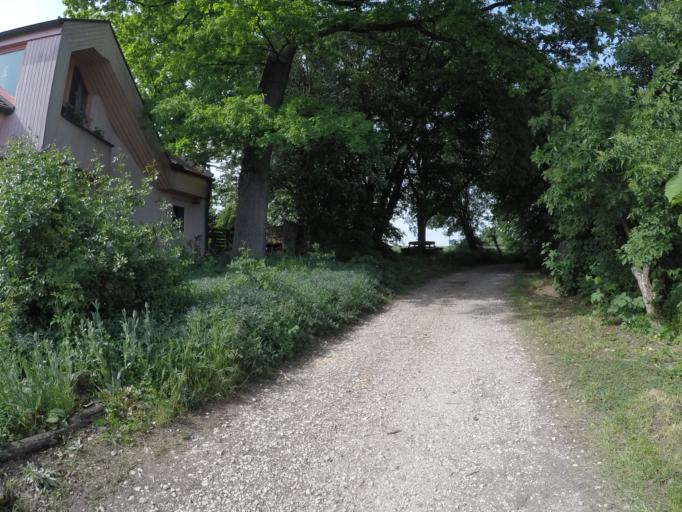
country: DE
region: Baden-Wuerttemberg
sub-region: Regierungsbezirk Stuttgart
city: Kongen
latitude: 48.6882
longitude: 9.3721
